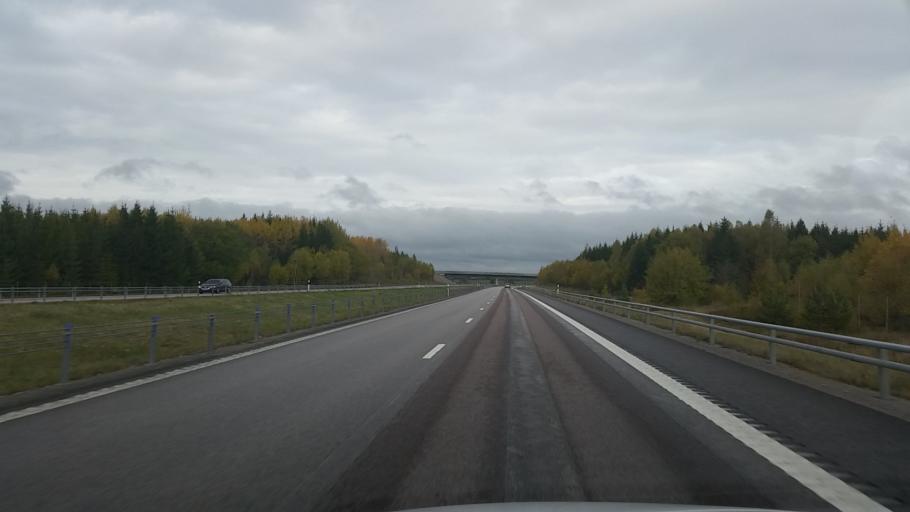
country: SE
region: Uppsala
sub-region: Osthammars Kommun
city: Bjorklinge
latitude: 60.0510
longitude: 17.6215
